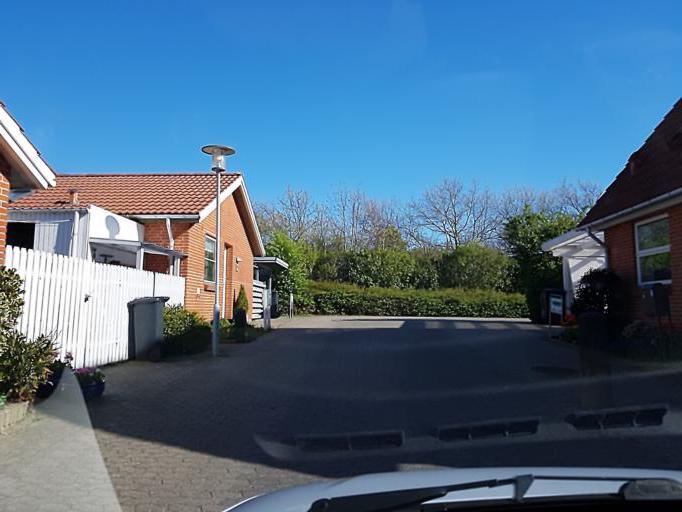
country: DK
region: South Denmark
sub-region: Esbjerg Kommune
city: Esbjerg
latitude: 55.5117
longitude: 8.4358
